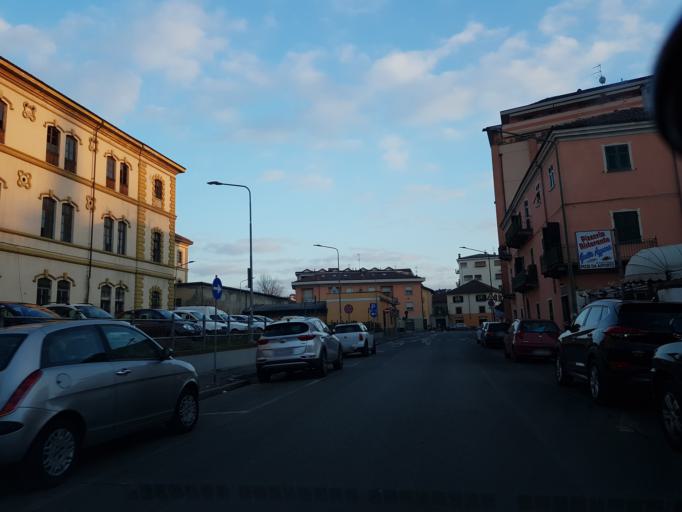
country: IT
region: Piedmont
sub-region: Provincia di Alessandria
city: Novi Ligure
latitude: 44.7615
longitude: 8.7916
